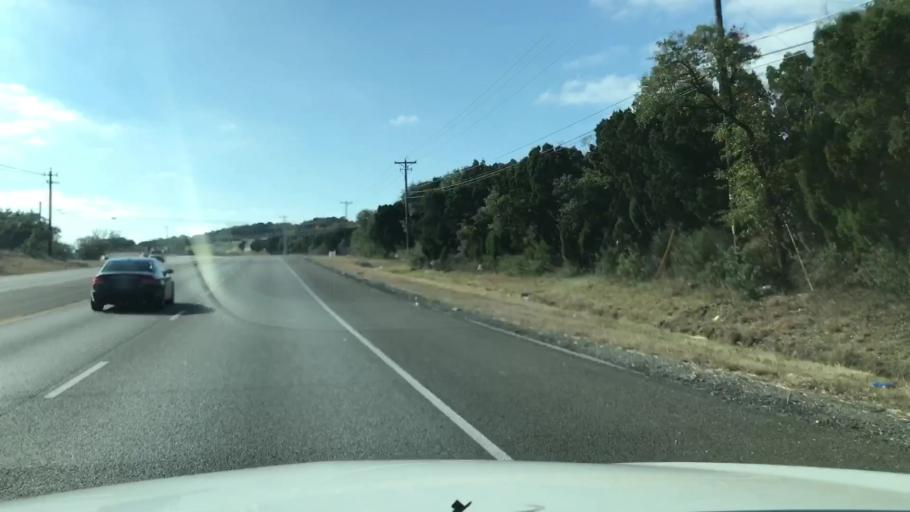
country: US
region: Texas
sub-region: Travis County
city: Bee Cave
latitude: 30.2828
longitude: -97.9174
